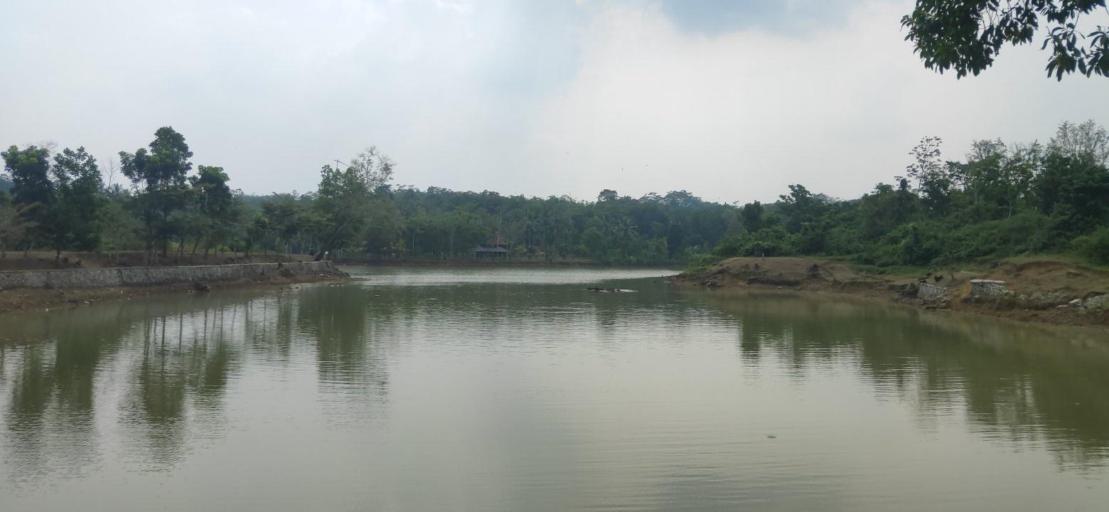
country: ID
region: West Java
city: Garisul
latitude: -6.4381
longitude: 106.5062
